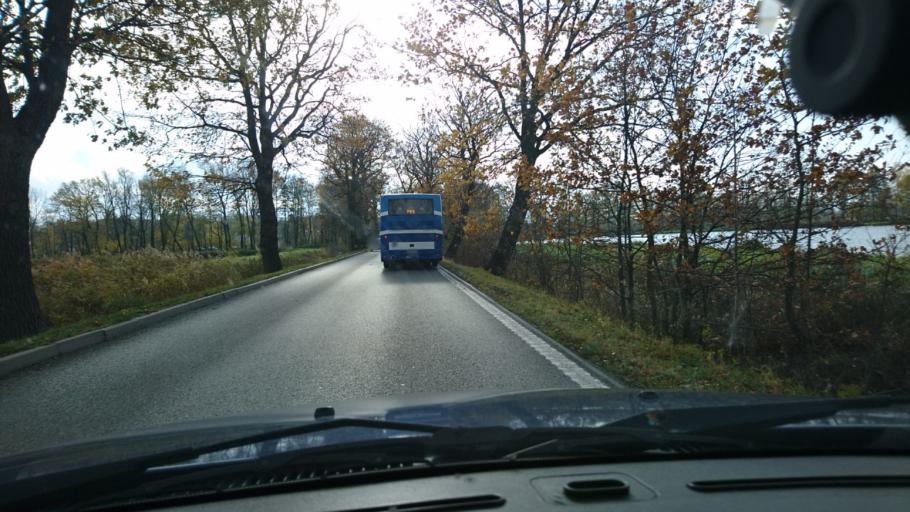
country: PL
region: Silesian Voivodeship
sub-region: Powiat bielski
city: Pisarzowice
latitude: 49.8953
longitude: 19.1443
